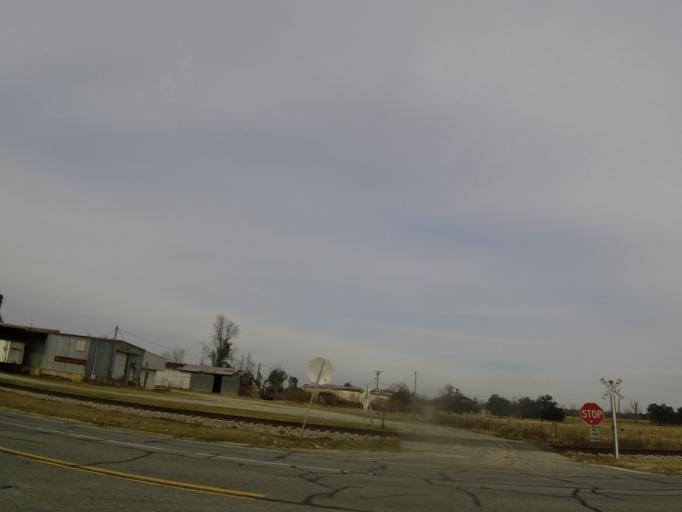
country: US
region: Georgia
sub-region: Seminole County
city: Donalsonville
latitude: 31.0352
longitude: -84.8634
